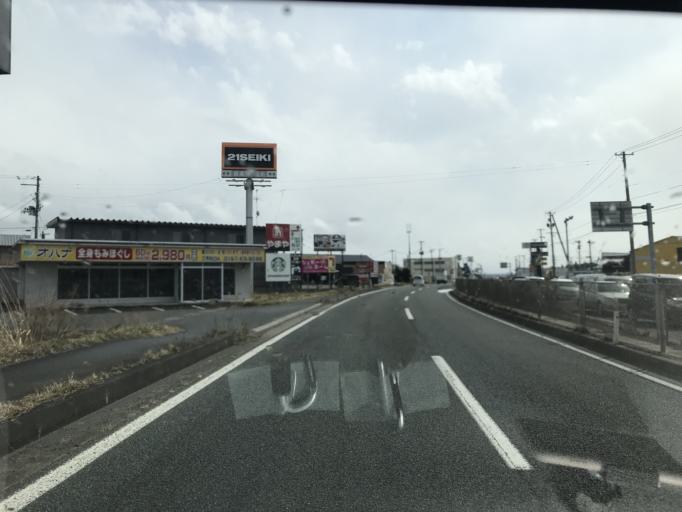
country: JP
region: Iwate
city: Kitakami
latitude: 39.3119
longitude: 141.1128
